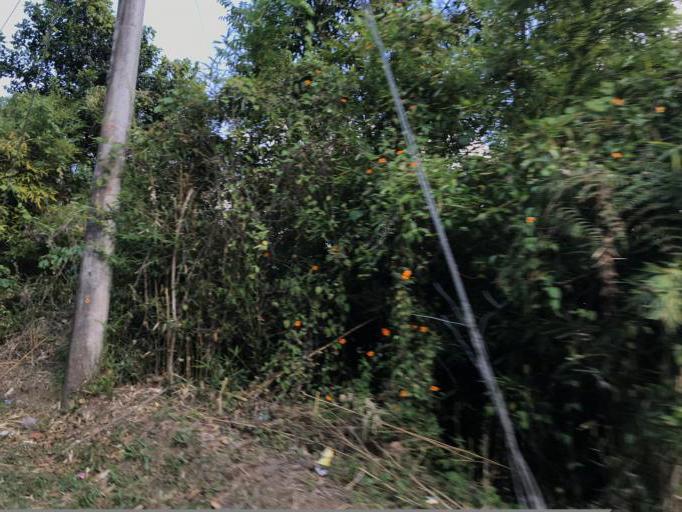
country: CO
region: Valle del Cauca
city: Cali
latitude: 3.4681
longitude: -76.6255
